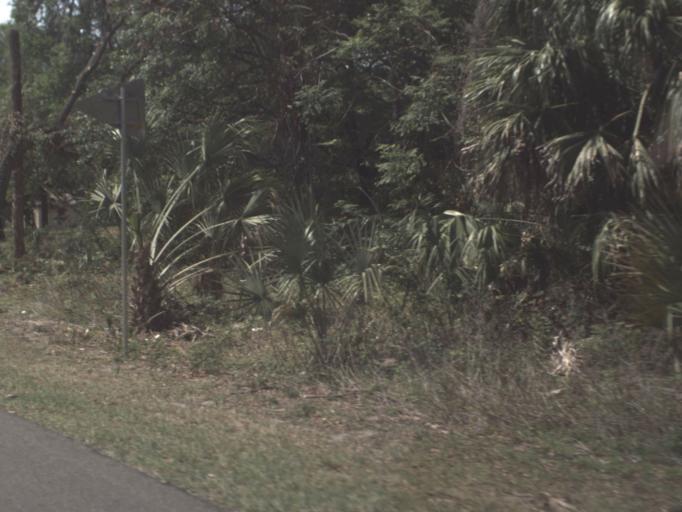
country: US
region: Florida
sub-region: Lake County
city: Umatilla
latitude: 28.9987
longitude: -81.6420
